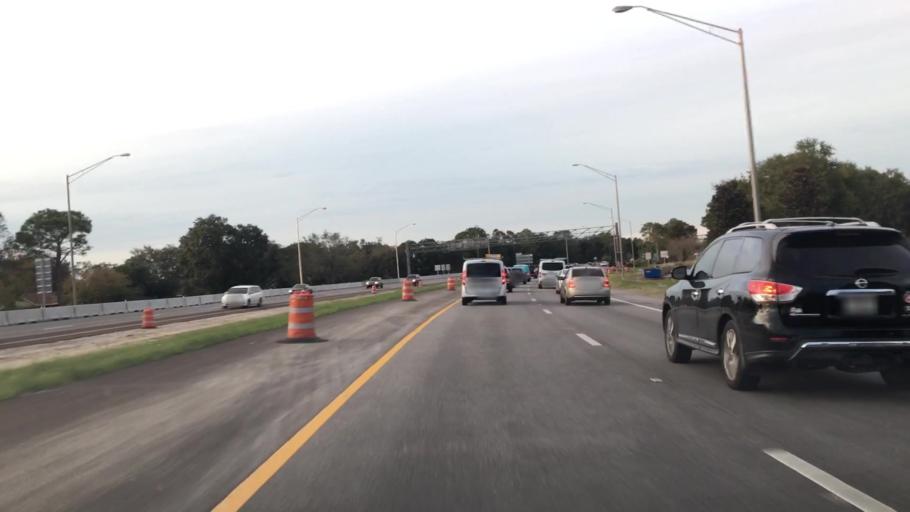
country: US
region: Florida
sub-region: Seminole County
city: Goldenrod
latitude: 28.6093
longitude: -81.2578
